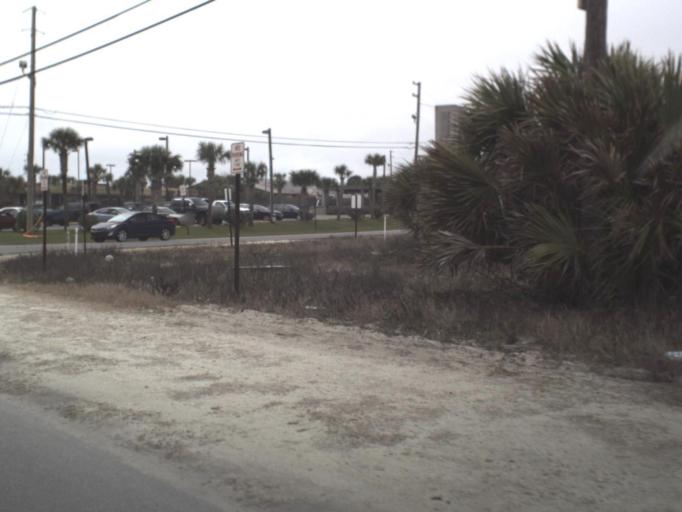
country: US
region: Florida
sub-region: Bay County
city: Laguna Beach
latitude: 30.2290
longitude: -85.9029
